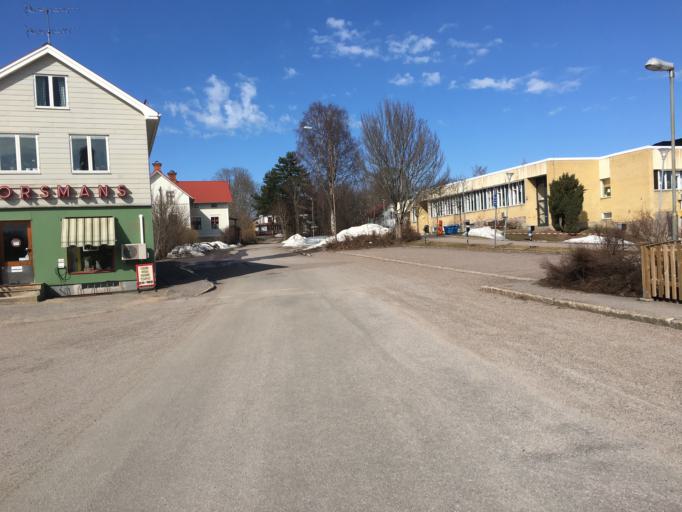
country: SE
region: Gaevleborg
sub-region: Hofors Kommun
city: Hofors
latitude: 60.5102
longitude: 16.4694
